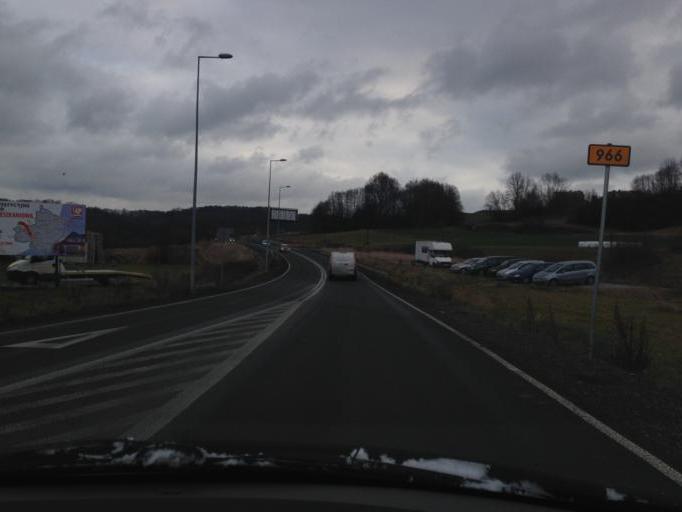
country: PL
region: Lesser Poland Voivodeship
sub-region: Powiat wielicki
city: Gdow
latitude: 49.8970
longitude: 20.2221
